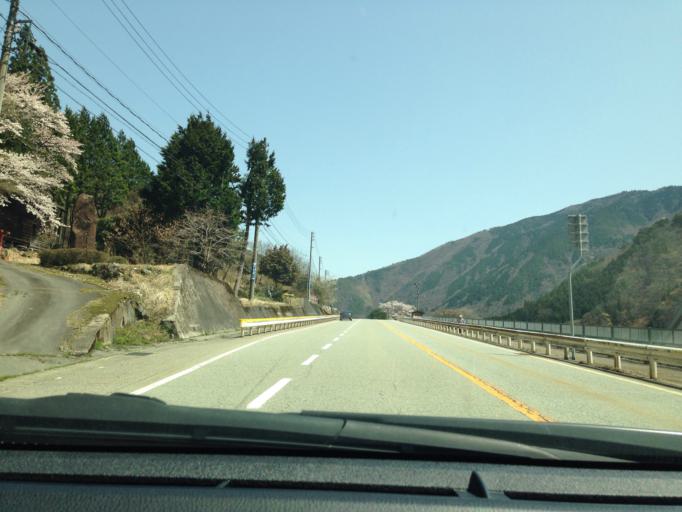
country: JP
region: Gifu
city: Takayama
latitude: 35.9953
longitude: 137.2807
